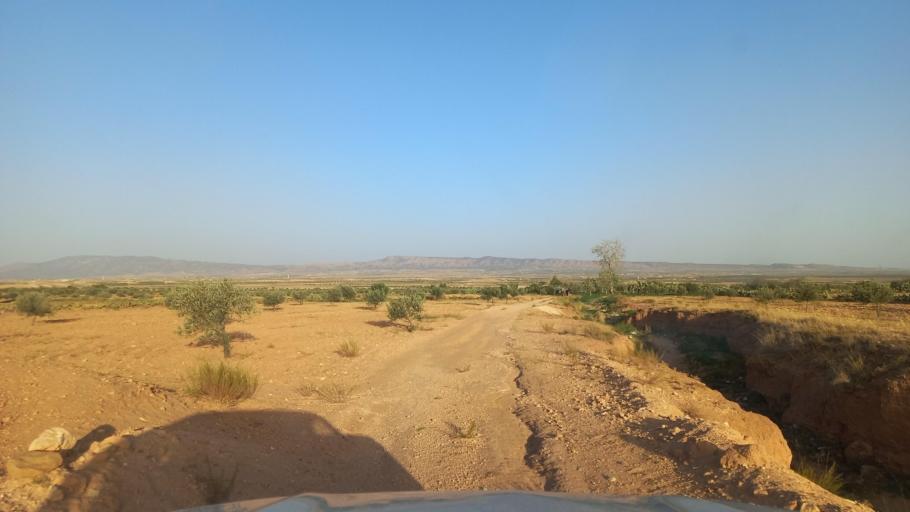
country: TN
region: Al Qasrayn
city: Sbiba
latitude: 35.3708
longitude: 9.0121
